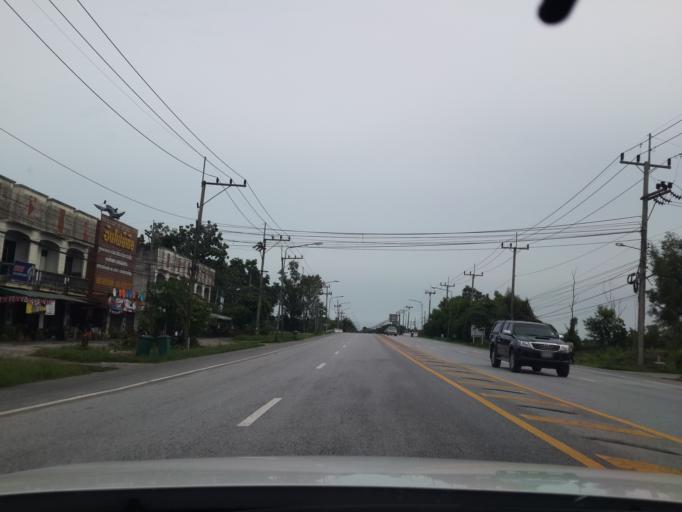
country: TH
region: Pattani
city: Nong Chik
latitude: 6.8039
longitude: 101.1523
